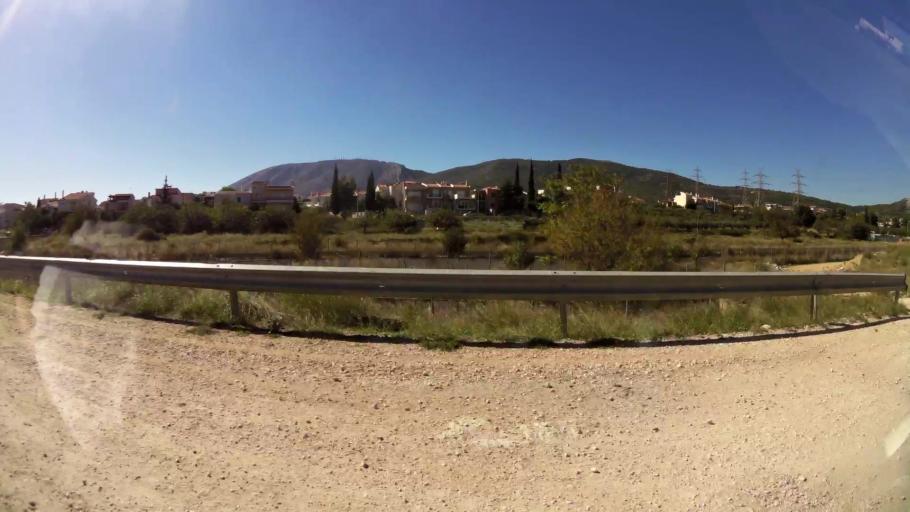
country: GR
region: Attica
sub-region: Nomarchia Anatolikis Attikis
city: Leondarion
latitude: 37.9932
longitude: 23.8634
